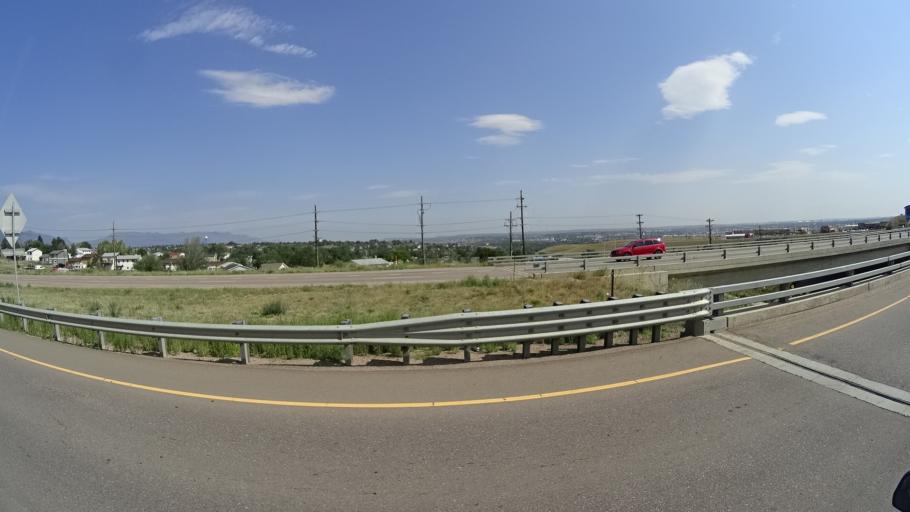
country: US
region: Colorado
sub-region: El Paso County
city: Stratmoor
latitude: 38.7656
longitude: -104.7894
